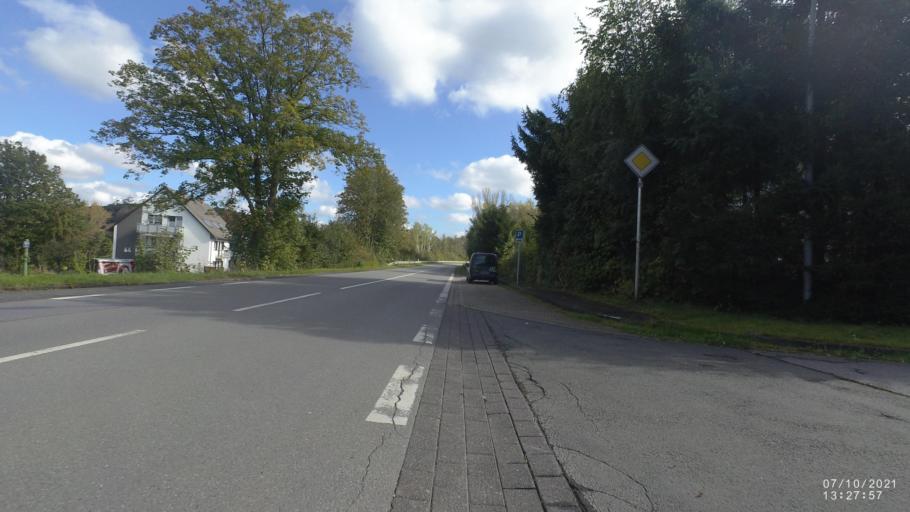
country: DE
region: North Rhine-Westphalia
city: Hemer
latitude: 51.4024
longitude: 7.7366
